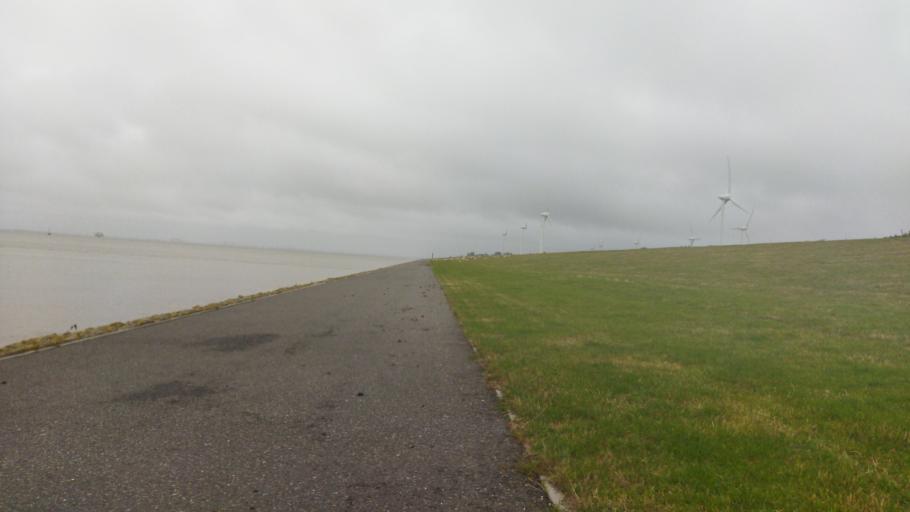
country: DE
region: Lower Saxony
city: Emden
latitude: 53.3349
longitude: 7.1029
